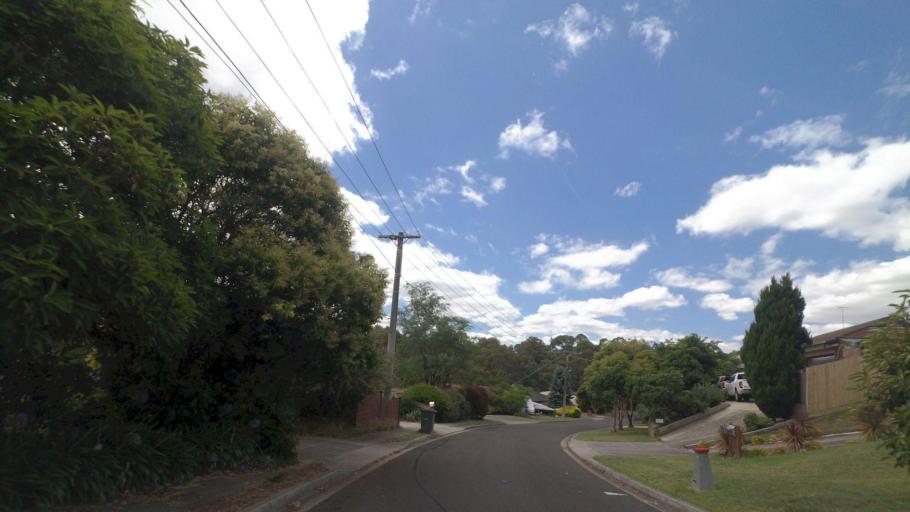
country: AU
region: Victoria
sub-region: Maroondah
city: Warranwood
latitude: -37.7708
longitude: 145.2426
